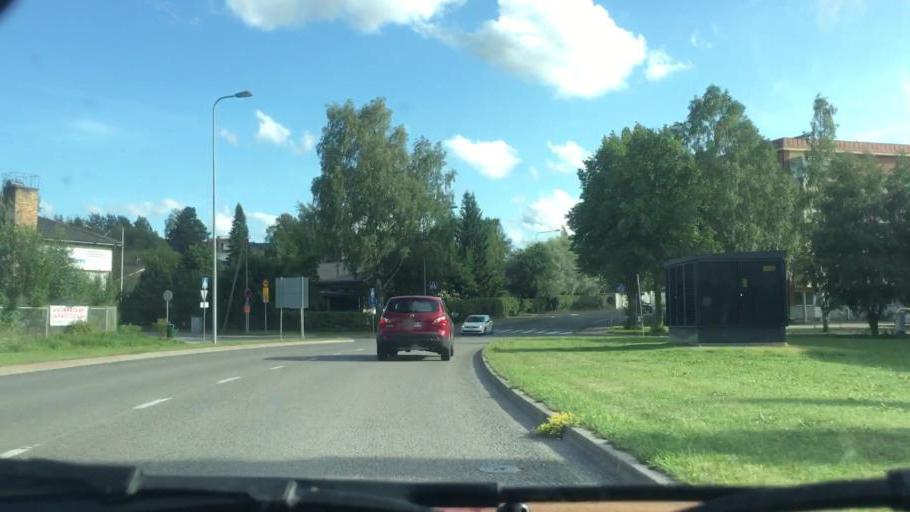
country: FI
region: Varsinais-Suomi
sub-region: Turku
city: Turku
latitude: 60.4603
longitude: 22.2467
